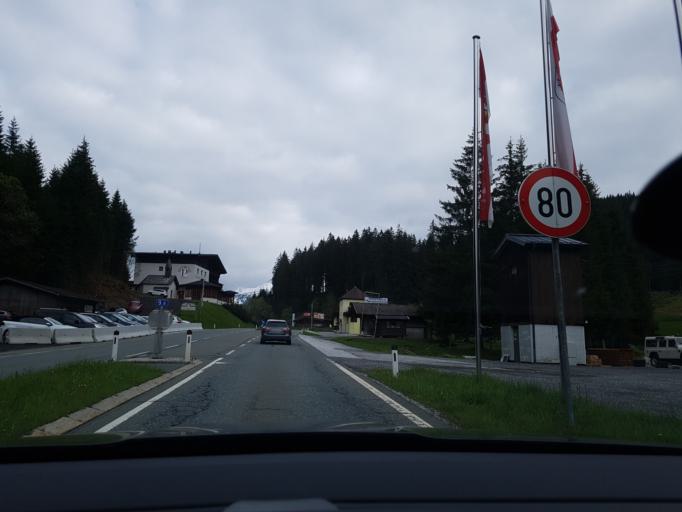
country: AT
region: Salzburg
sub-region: Politischer Bezirk Zell am See
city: Hollersbach im Pinzgau
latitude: 47.3100
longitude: 12.4074
